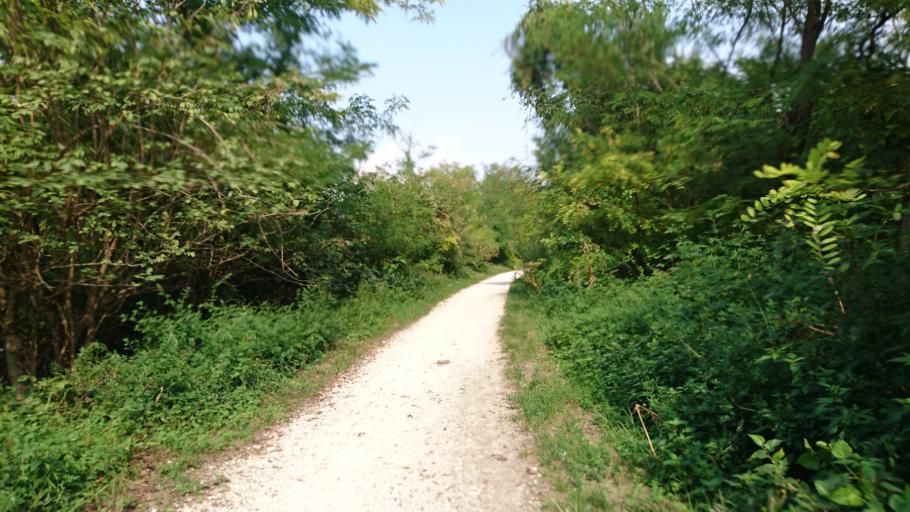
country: IT
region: Veneto
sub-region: Provincia di Padova
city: Saletto
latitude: 45.4563
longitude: 11.8594
